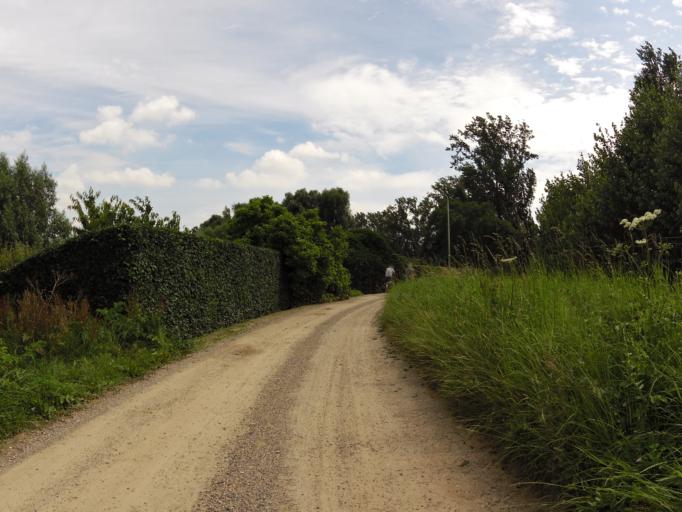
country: NL
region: South Holland
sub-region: Gemeente Leerdam
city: Leerdam
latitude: 51.8735
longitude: 5.1227
